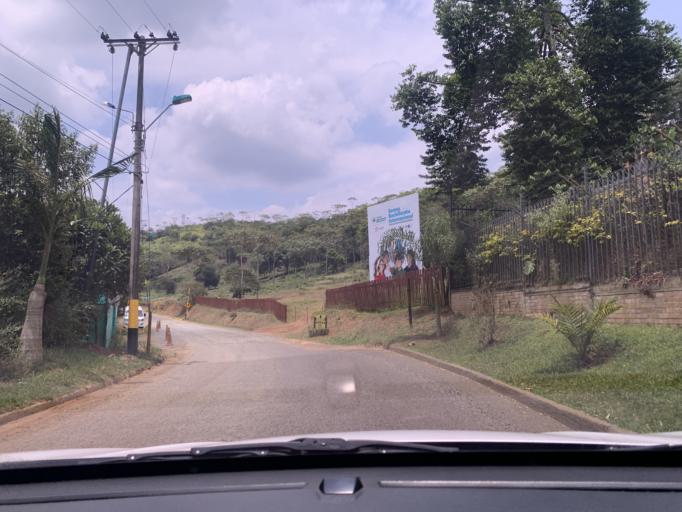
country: CO
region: Valle del Cauca
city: Jamundi
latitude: 3.3394
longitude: -76.5539
